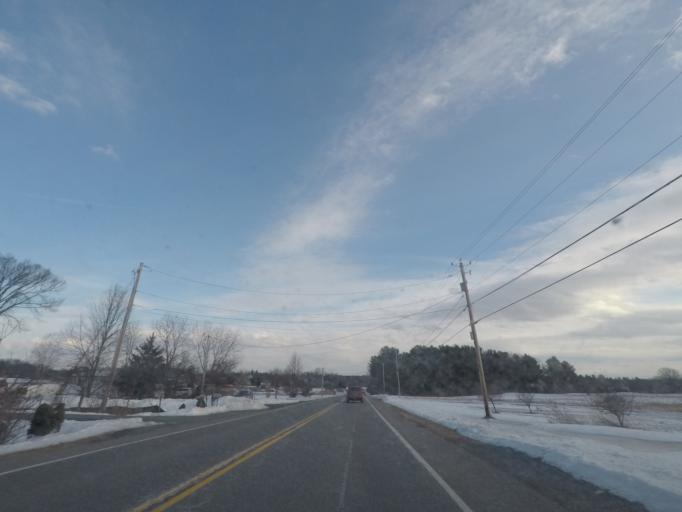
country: US
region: New York
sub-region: Schenectady County
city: Niskayuna
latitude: 42.8378
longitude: -73.8557
